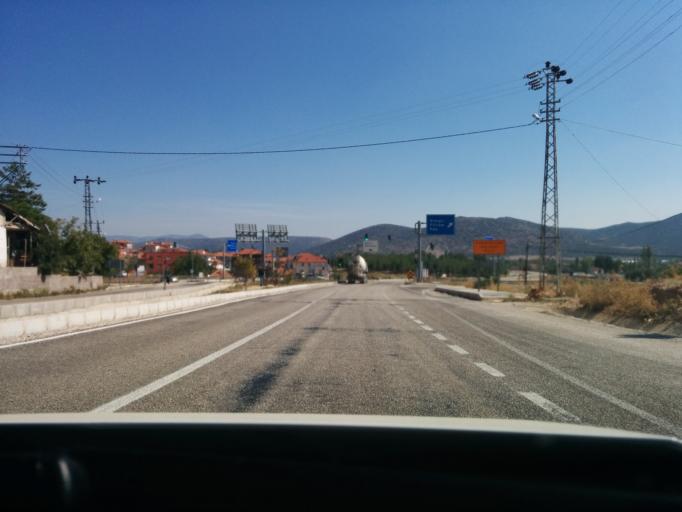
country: TR
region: Antalya
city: Korkuteli
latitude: 37.0540
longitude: 30.1866
